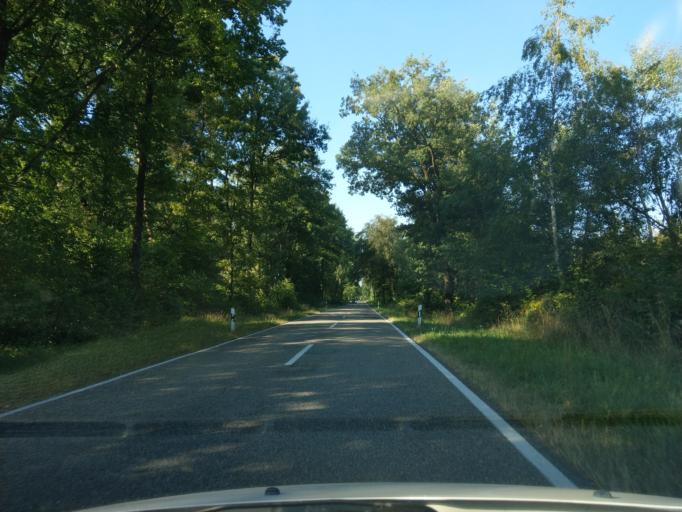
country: DE
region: Baden-Wuerttemberg
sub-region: Karlsruhe Region
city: Hugelsheim
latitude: 48.7641
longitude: 8.0903
